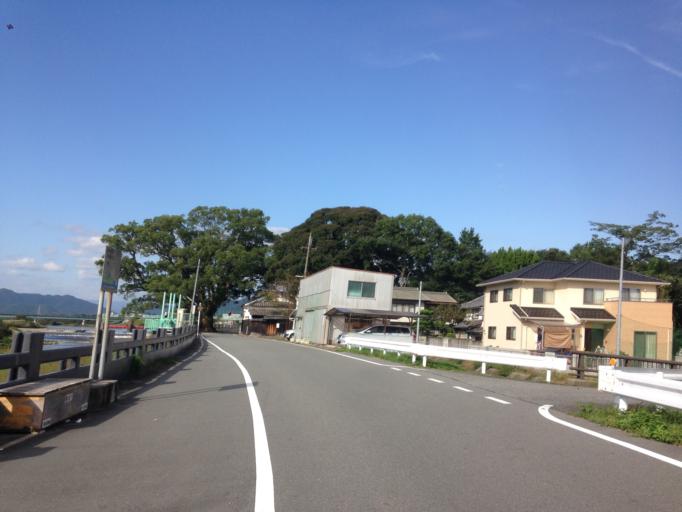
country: JP
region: Hyogo
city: Tatsunocho-tominaga
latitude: 34.8678
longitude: 134.5511
